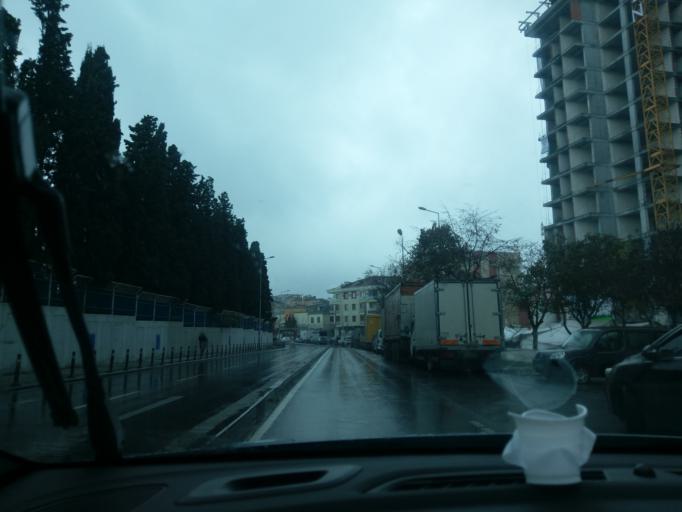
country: TR
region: Istanbul
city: Sisli
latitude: 41.0895
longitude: 28.9678
